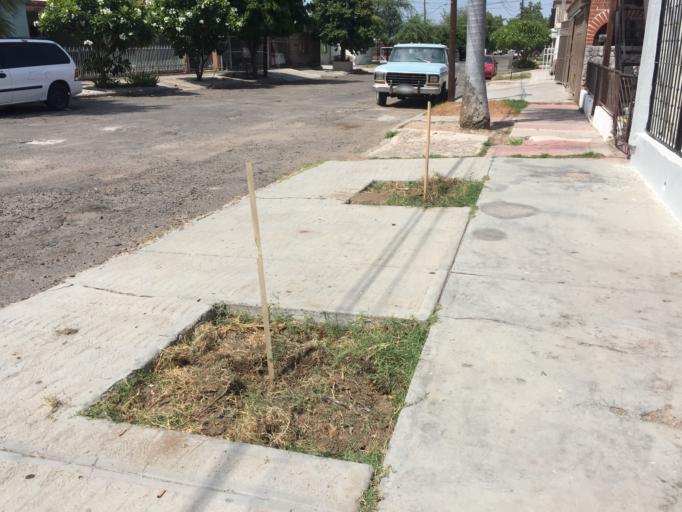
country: MX
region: Sonora
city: Hermosillo
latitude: 29.1045
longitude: -110.9655
